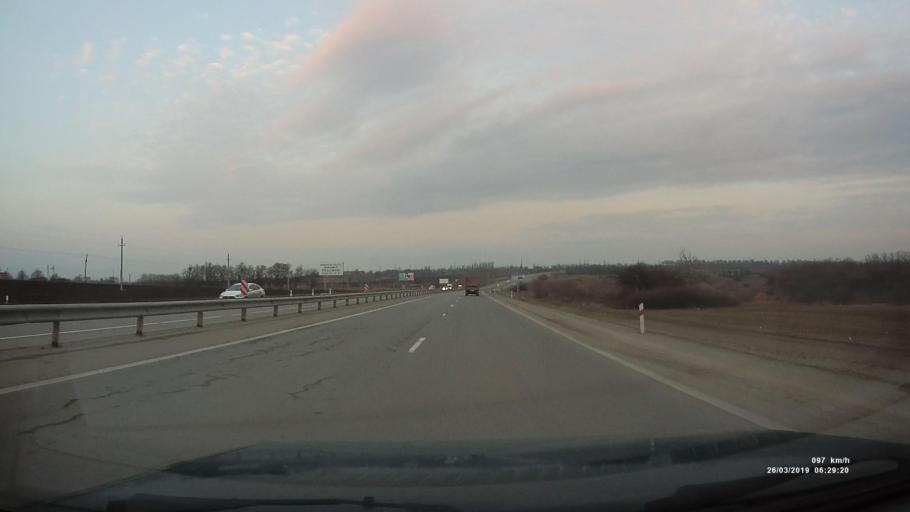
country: RU
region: Rostov
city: Kalinin
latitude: 47.2671
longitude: 39.5761
